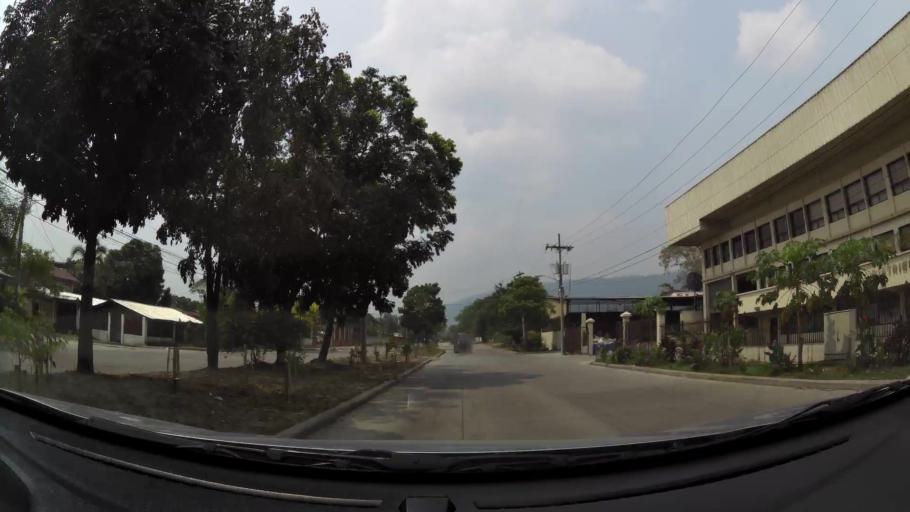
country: HN
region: Cortes
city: San Pedro Sula
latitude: 15.4807
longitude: -88.0256
